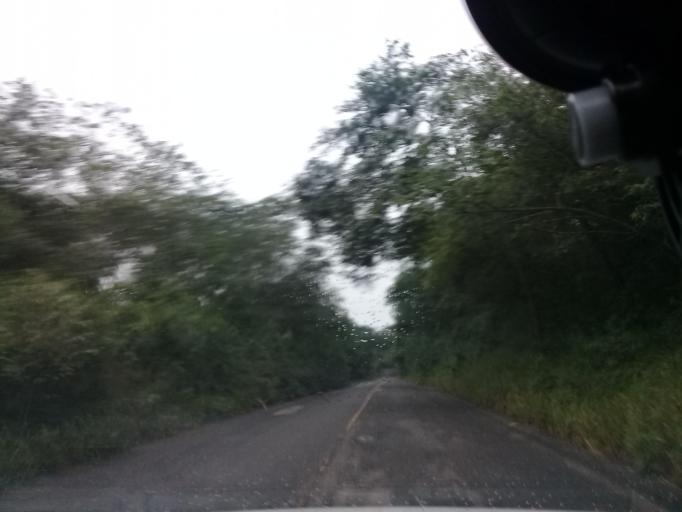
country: MX
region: Veracruz
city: Platon Sanchez
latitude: 21.2350
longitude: -98.3687
